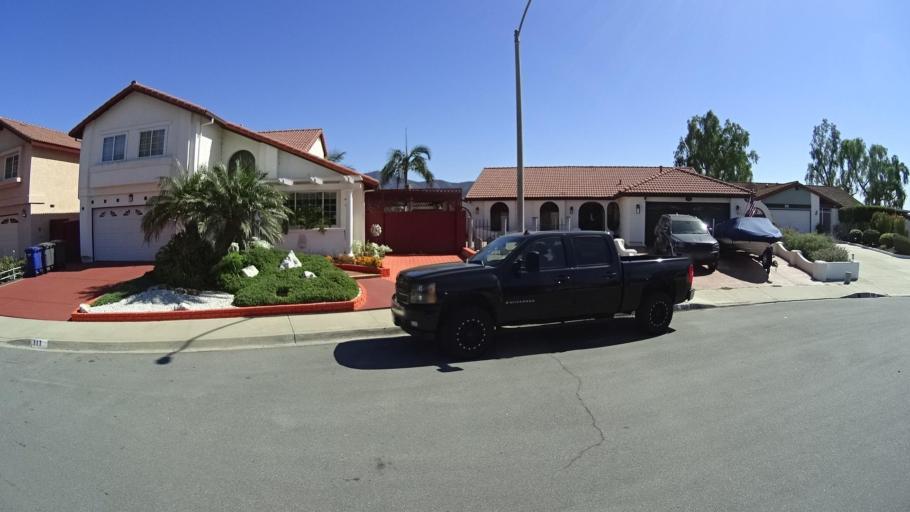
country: US
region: California
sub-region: San Diego County
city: La Presa
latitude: 32.6956
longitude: -117.0049
